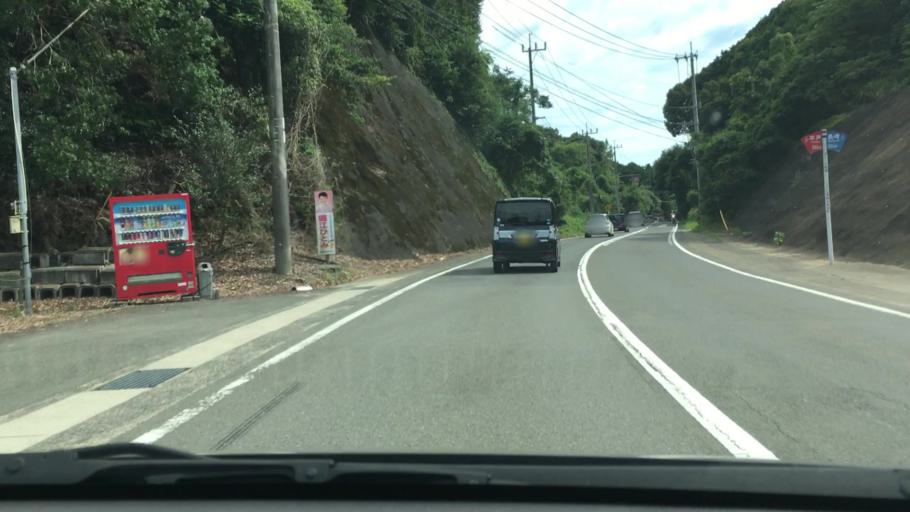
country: JP
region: Nagasaki
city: Togitsu
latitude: 32.9221
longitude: 129.7877
